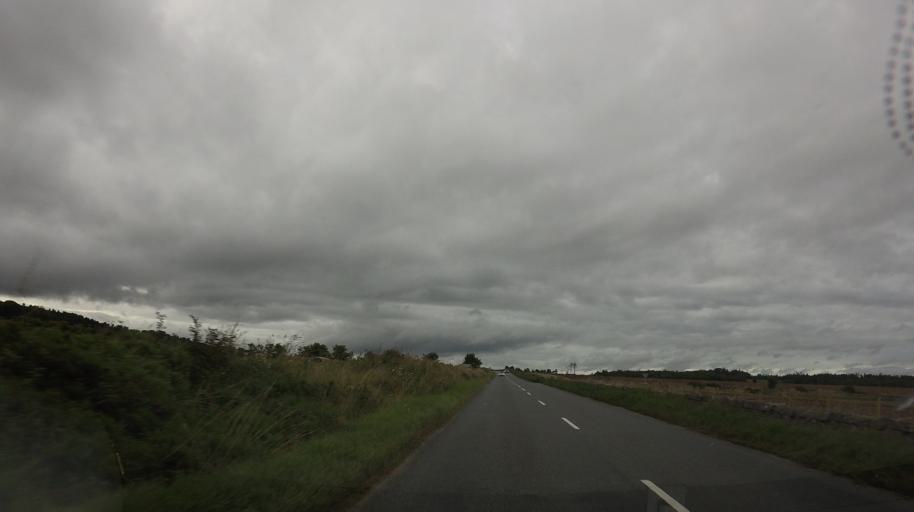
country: GB
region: Scotland
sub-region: Aberdeenshire
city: Kemnay
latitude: 57.1463
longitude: -2.4348
